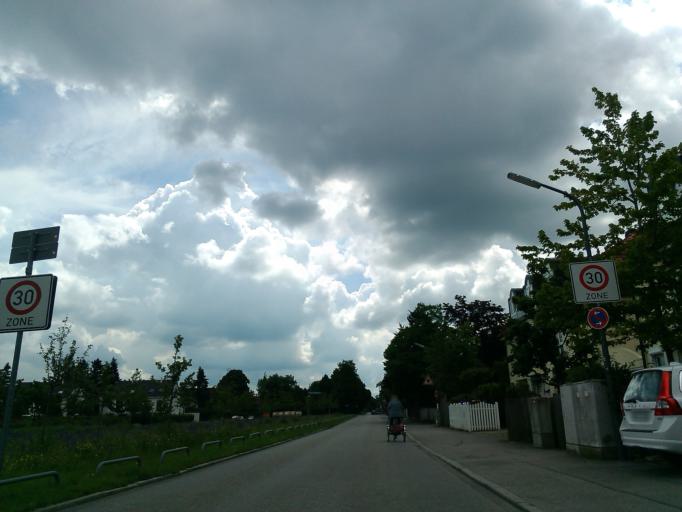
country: DE
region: Bavaria
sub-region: Upper Bavaria
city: Neubiberg
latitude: 48.1170
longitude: 11.6569
